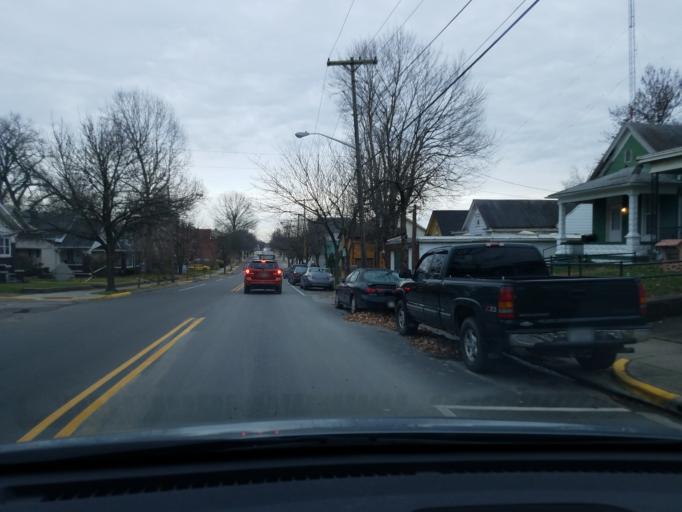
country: US
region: Indiana
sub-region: Floyd County
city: New Albany
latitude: 38.3014
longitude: -85.8149
